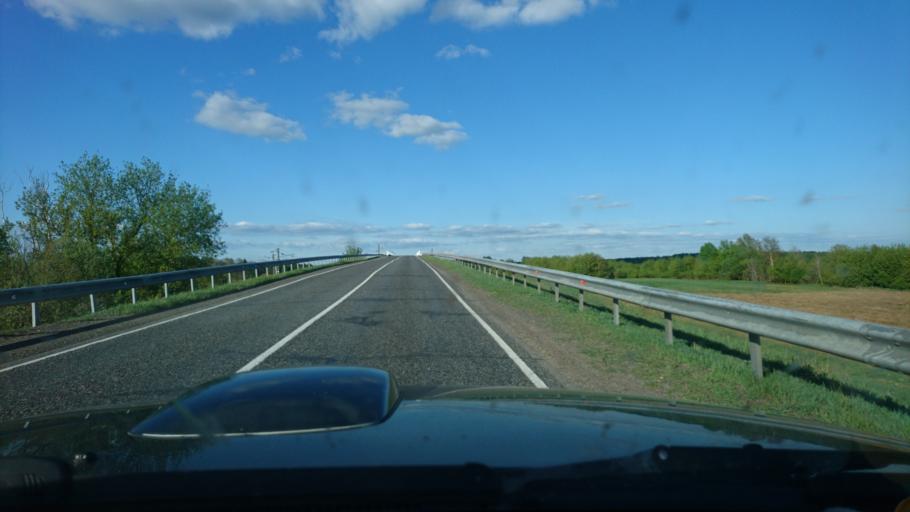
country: BY
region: Brest
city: Nyakhachava
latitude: 52.6377
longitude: 25.1929
